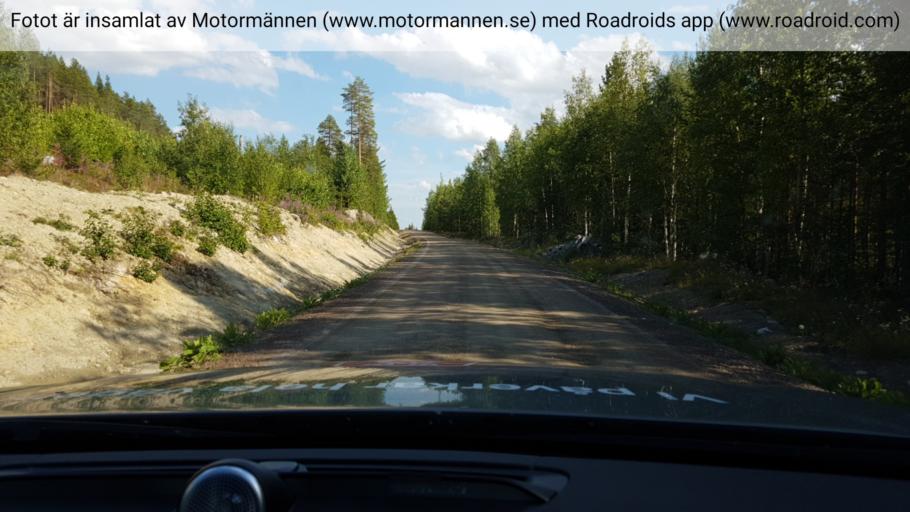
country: SE
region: Jaemtland
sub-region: Stroemsunds Kommun
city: Stroemsund
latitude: 63.9856
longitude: 16.0107
